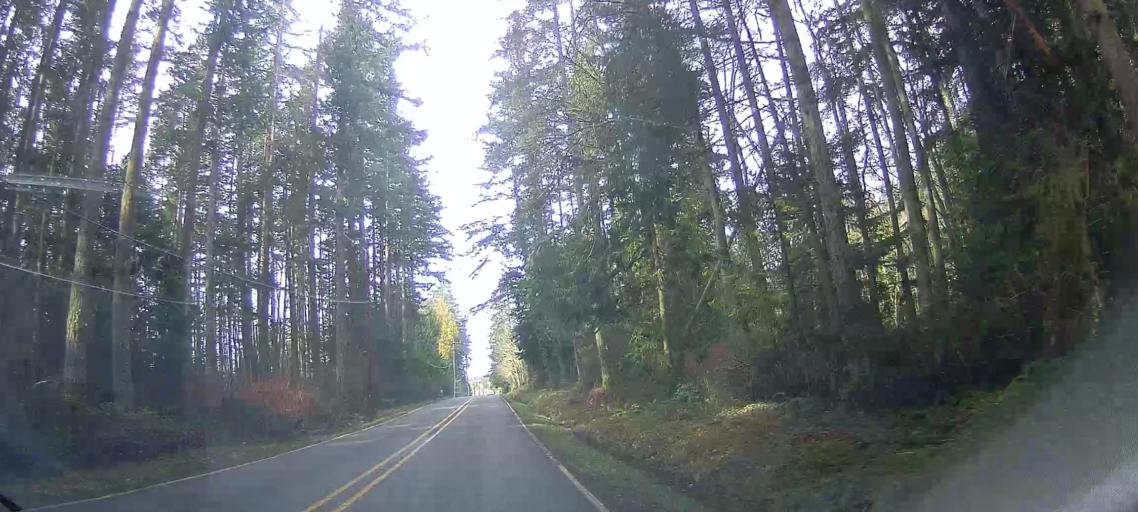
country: US
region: Washington
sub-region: Island County
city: Camano
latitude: 48.1521
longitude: -122.5134
